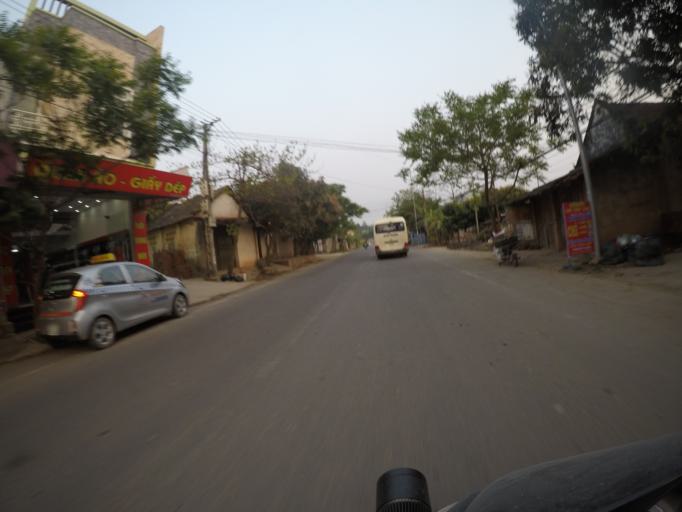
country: VN
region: Vinh Phuc
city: Trai Ngau
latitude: 21.4242
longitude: 105.5953
